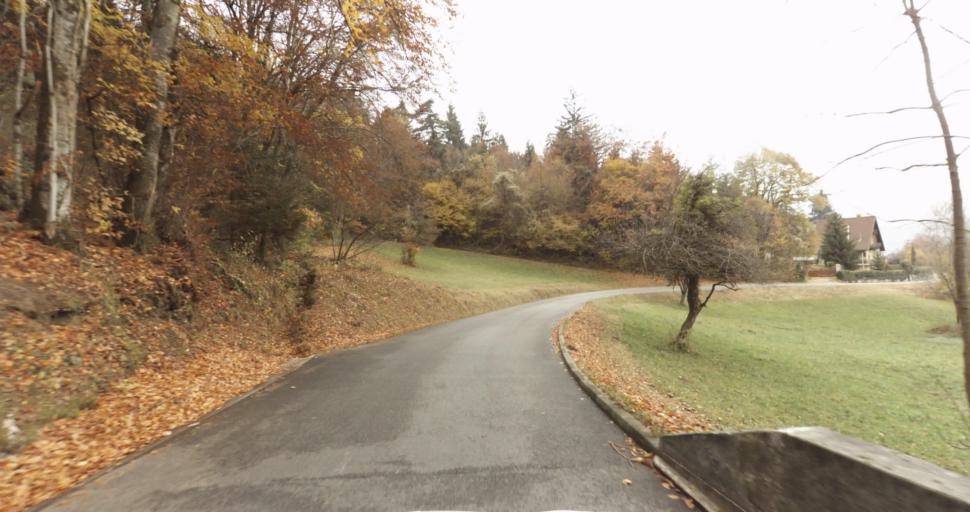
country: FR
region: Rhone-Alpes
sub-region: Departement de la Haute-Savoie
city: Talloires
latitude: 45.8163
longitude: 6.1948
